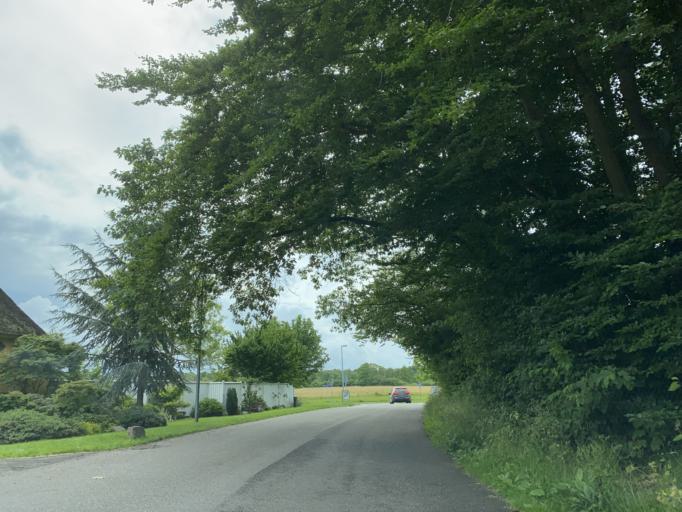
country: DK
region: South Denmark
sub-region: Sonderborg Kommune
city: Sonderborg
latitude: 54.9151
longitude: 9.8280
